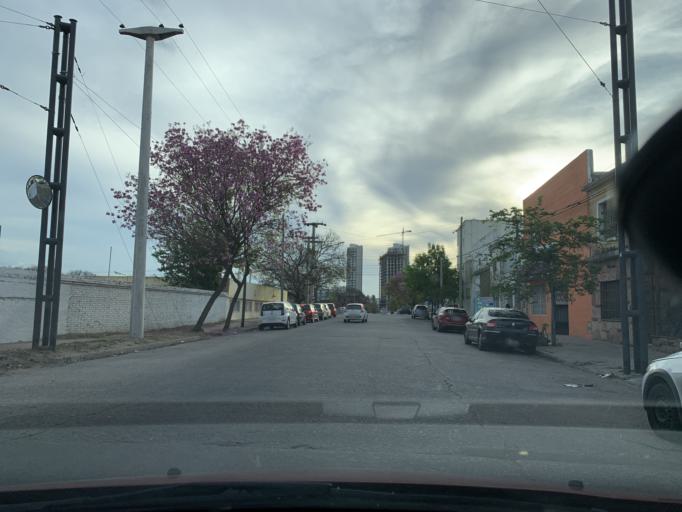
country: AR
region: Cordoba
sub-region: Departamento de Capital
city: Cordoba
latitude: -31.4083
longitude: -64.1672
